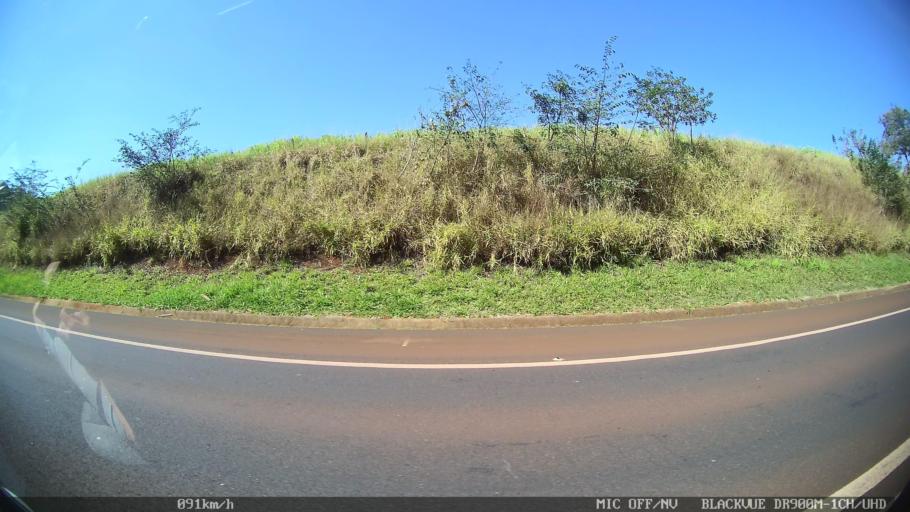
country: BR
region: Sao Paulo
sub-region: Franca
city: Franca
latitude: -20.6302
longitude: -47.4657
